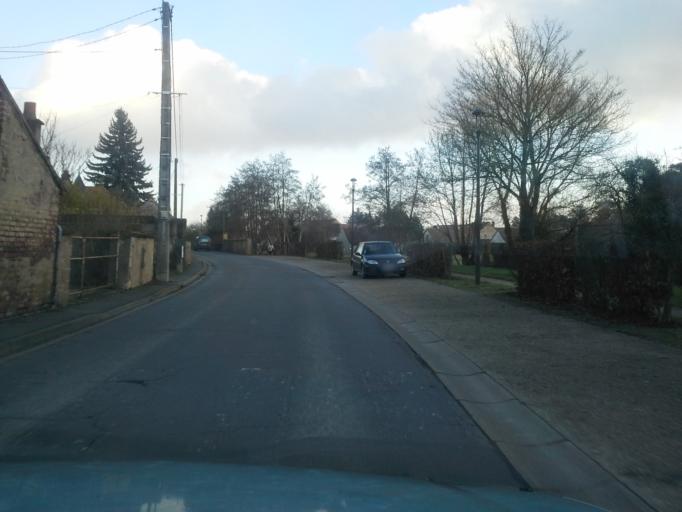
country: FR
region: Centre
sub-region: Departement du Loir-et-Cher
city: Naveil
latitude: 47.8033
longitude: 1.0386
